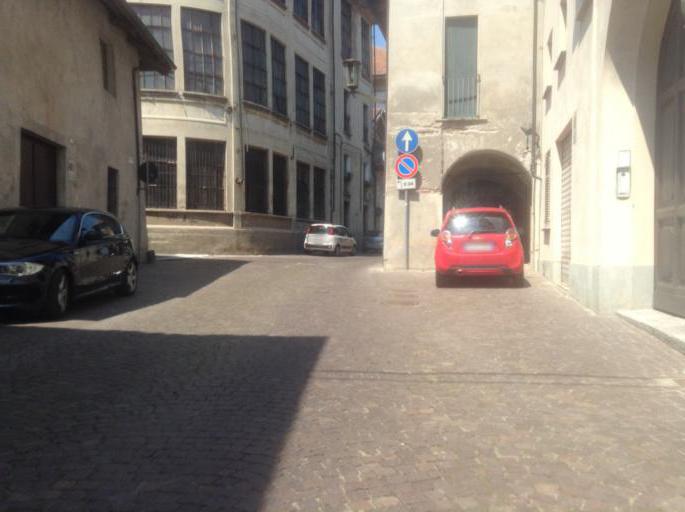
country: IT
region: Piedmont
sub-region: Provincia di Torino
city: Carignano
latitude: 44.9071
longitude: 7.6759
